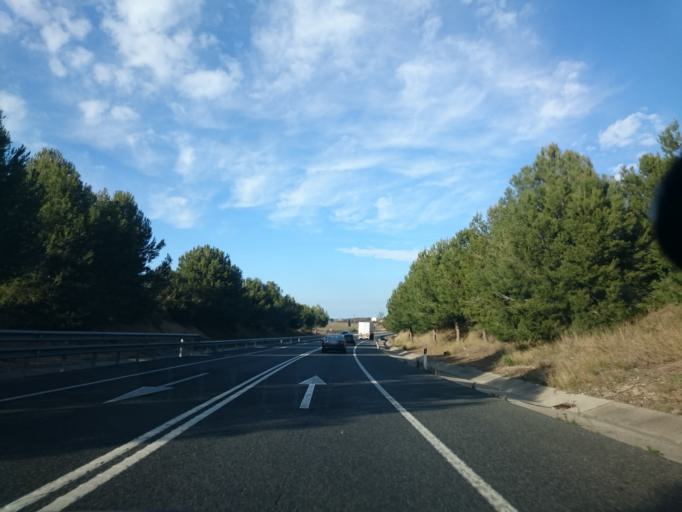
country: ES
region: Catalonia
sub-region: Provincia de Barcelona
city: Castellet
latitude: 41.3050
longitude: 1.6345
